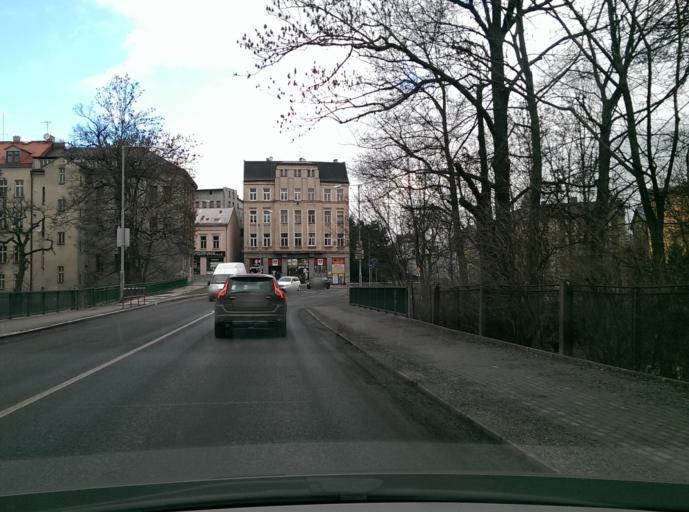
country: CZ
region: Liberecky
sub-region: Okres Jablonec nad Nisou
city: Jablonec nad Nisou
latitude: 50.7233
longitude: 15.1766
